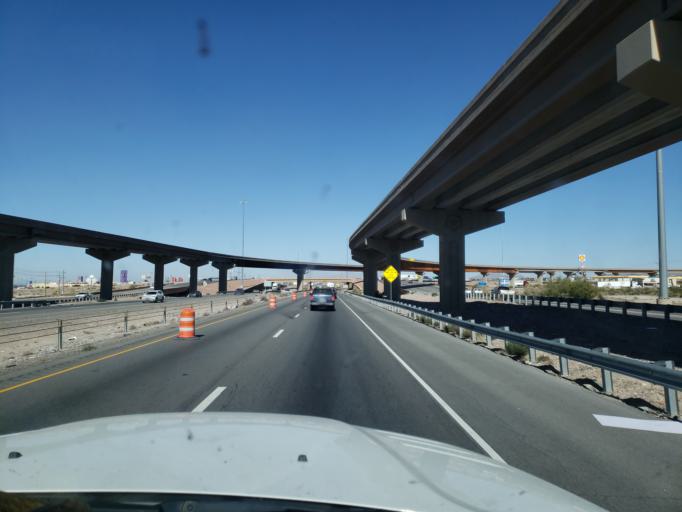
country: US
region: Texas
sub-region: El Paso County
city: Canutillo
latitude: 31.9048
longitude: -106.5827
